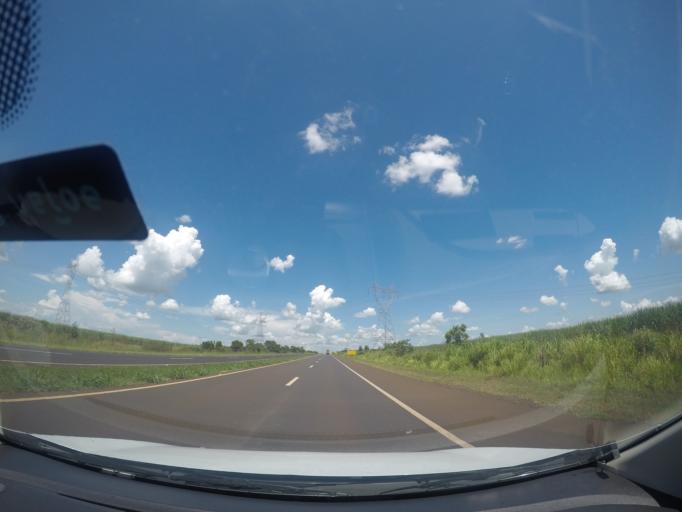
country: BR
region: Minas Gerais
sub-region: Prata
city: Prata
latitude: -19.6669
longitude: -48.7780
